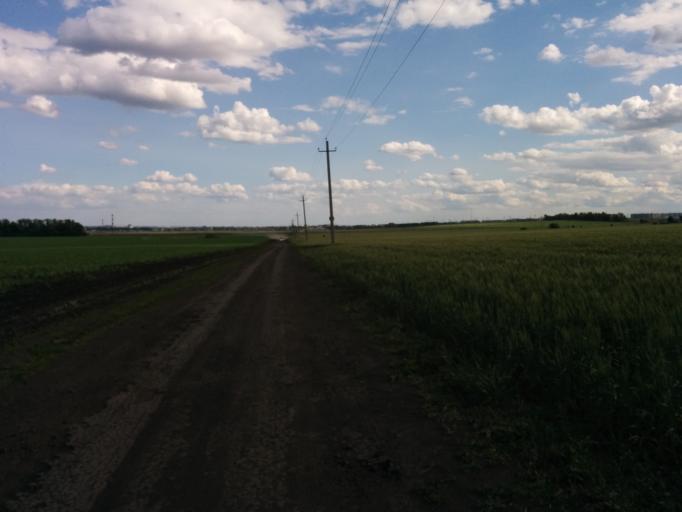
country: RU
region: Tambov
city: Donskoye
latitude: 52.7971
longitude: 41.4271
